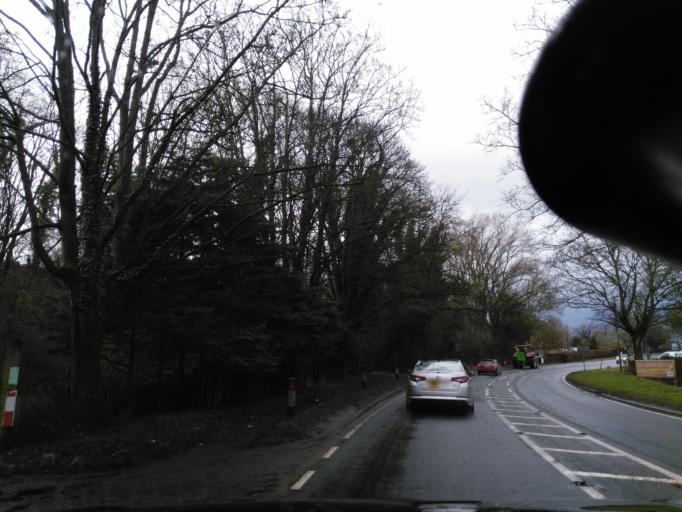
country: GB
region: England
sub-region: North Yorkshire
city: Ripon
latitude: 54.0640
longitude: -1.5381
